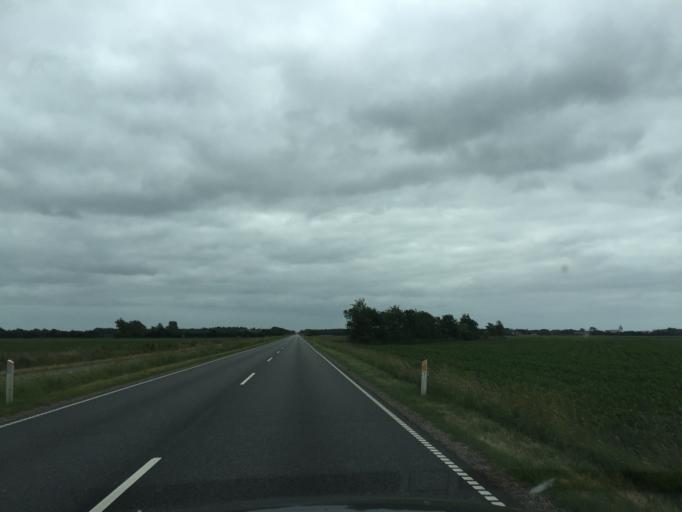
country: DK
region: South Denmark
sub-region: Esbjerg Kommune
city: Ribe
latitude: 55.2482
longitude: 8.7232
